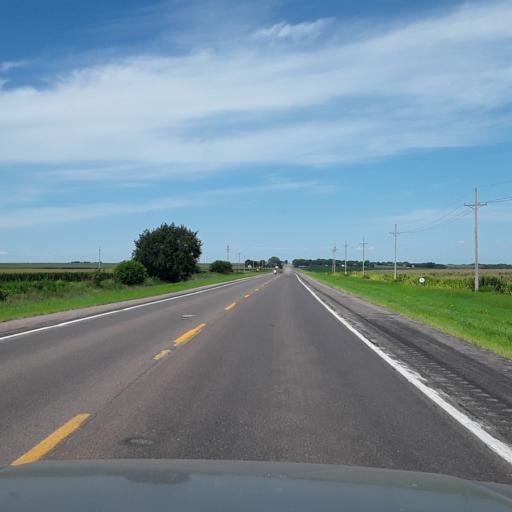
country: US
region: Nebraska
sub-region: Seward County
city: Seward
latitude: 40.9018
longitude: -97.1161
